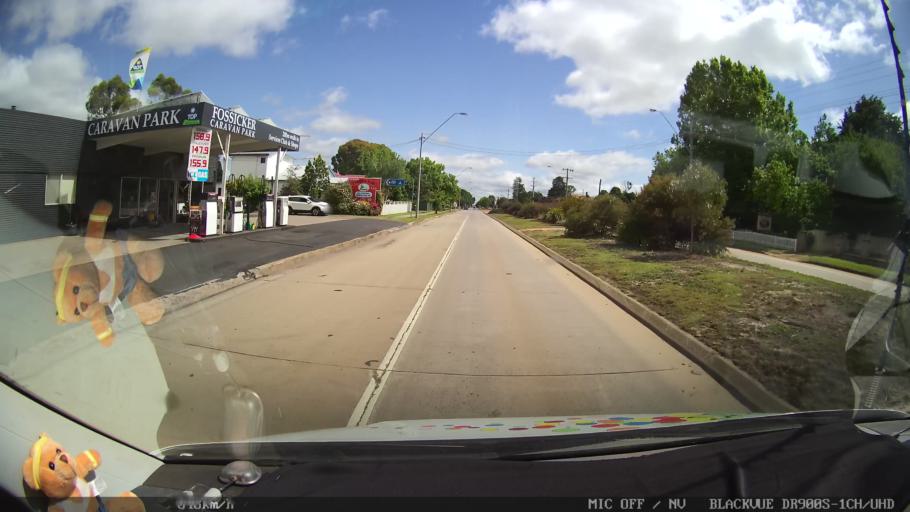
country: AU
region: New South Wales
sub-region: Glen Innes Severn
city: Glen Innes
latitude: -29.7449
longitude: 151.7368
